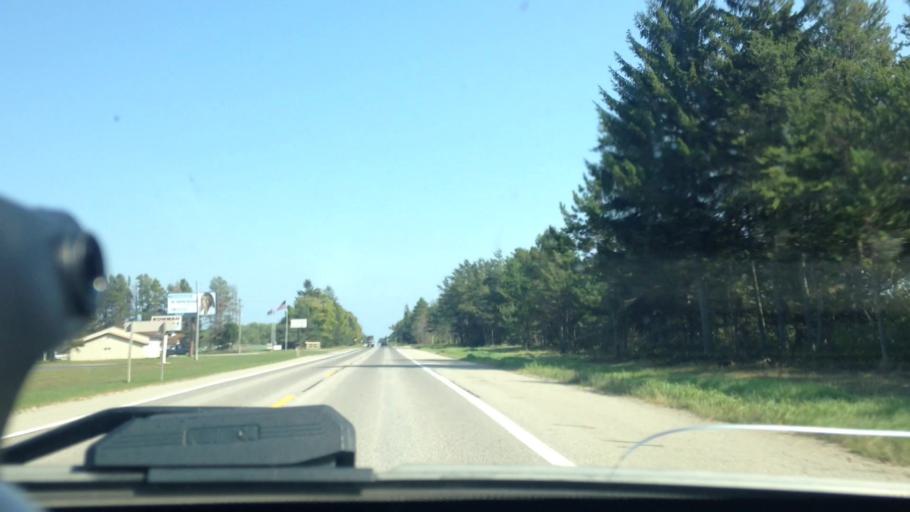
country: US
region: Michigan
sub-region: Luce County
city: Newberry
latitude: 46.3034
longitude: -85.4707
